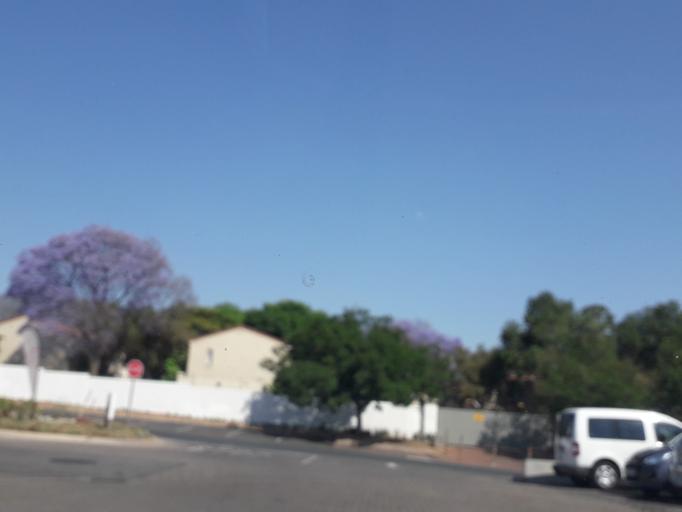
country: ZA
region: Gauteng
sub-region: City of Johannesburg Metropolitan Municipality
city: Midrand
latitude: -26.0631
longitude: 28.0256
